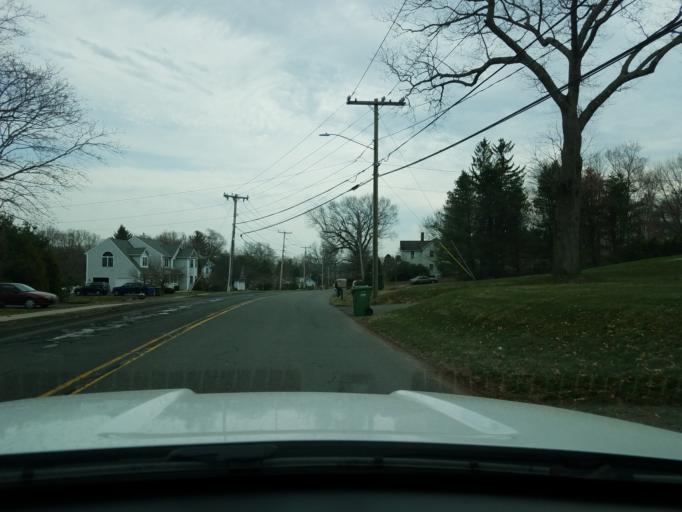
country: US
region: Connecticut
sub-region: Middlesex County
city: Cromwell
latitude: 41.6141
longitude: -72.6669
